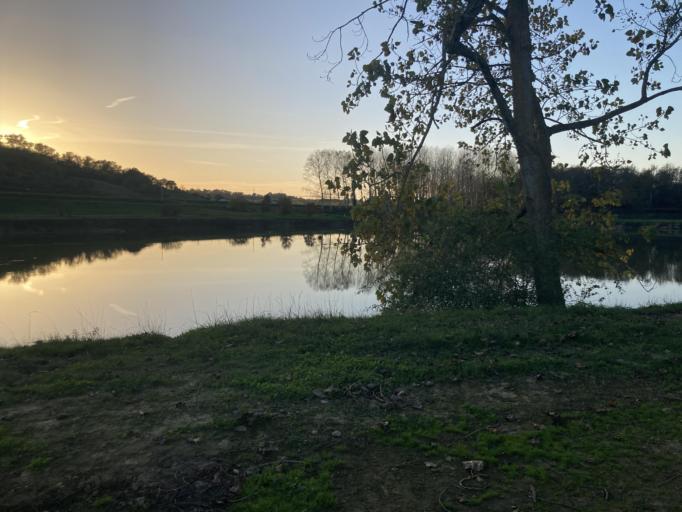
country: FR
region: Aquitaine
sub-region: Departement des Landes
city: Mugron
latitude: 43.7590
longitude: -0.7296
